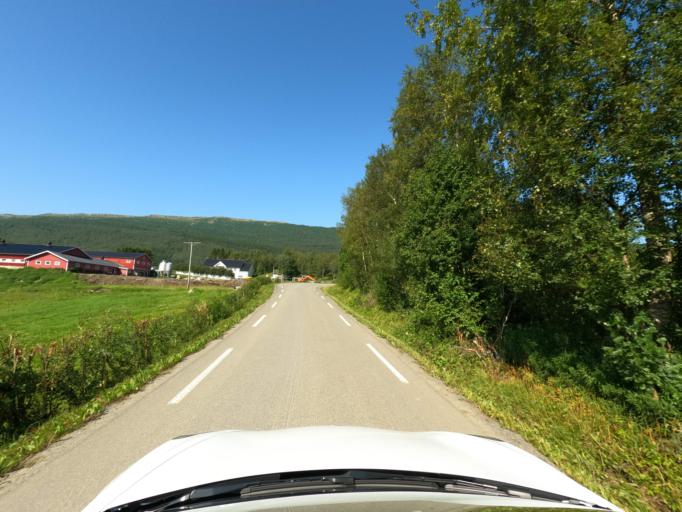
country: NO
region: Nordland
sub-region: Ballangen
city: Ballangen
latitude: 68.3459
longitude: 16.8060
